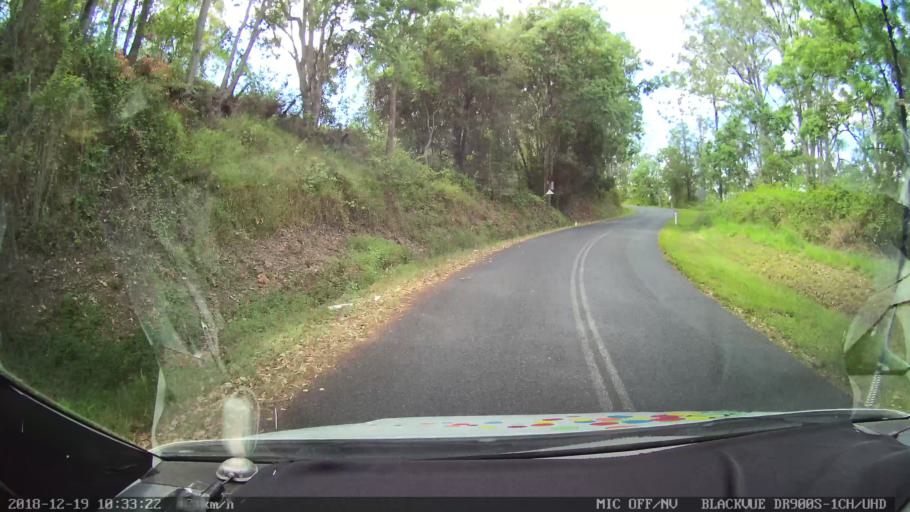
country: AU
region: New South Wales
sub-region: Lismore Municipality
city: Larnook
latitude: -28.5767
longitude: 153.1262
